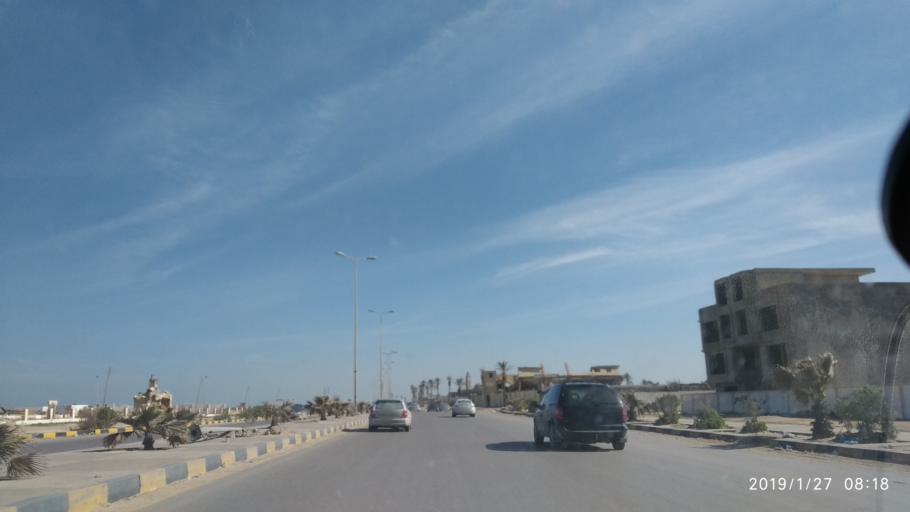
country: LY
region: Tripoli
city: Tagiura
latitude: 32.8952
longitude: 13.3308
